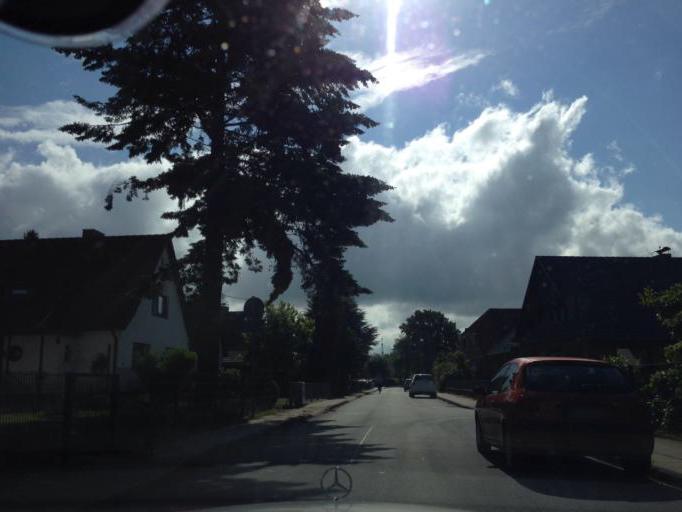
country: DE
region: Schleswig-Holstein
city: Barsbuettel
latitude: 53.5716
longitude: 10.1724
